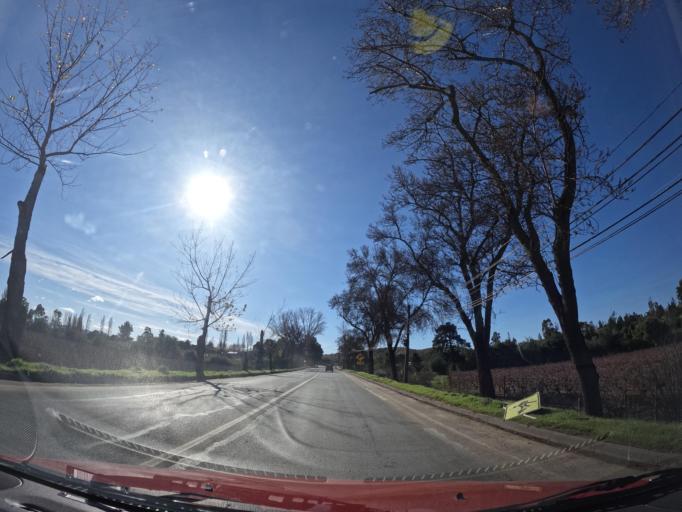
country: CL
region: Maule
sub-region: Provincia de Cauquenes
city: Cauquenes
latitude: -35.9576
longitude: -72.3114
